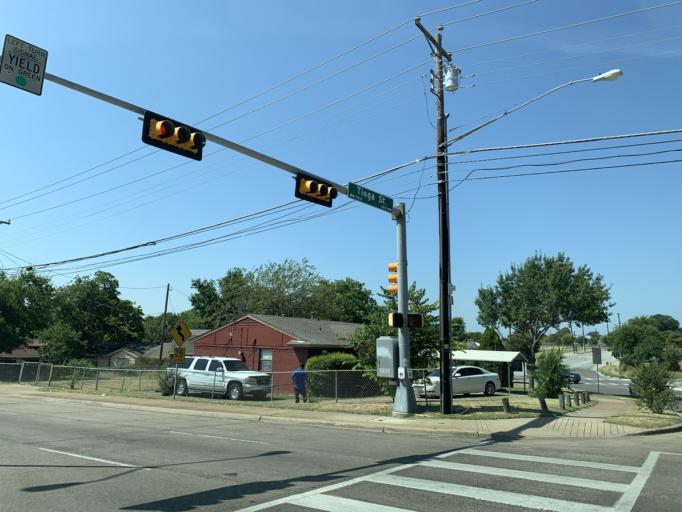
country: US
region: Texas
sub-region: Dallas County
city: Hutchins
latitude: 32.6643
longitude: -96.7572
